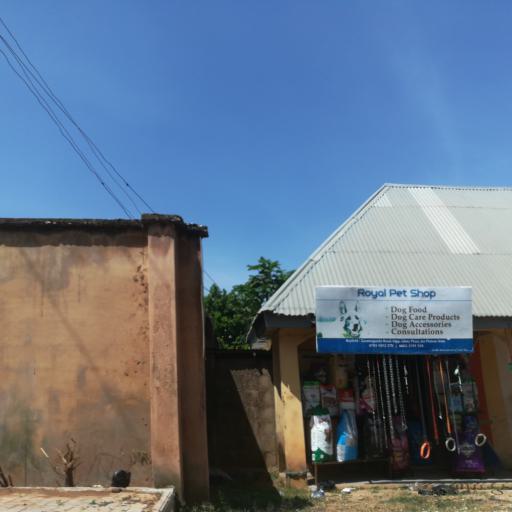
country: NG
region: Plateau
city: Bukuru
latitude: 9.8469
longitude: 8.8735
